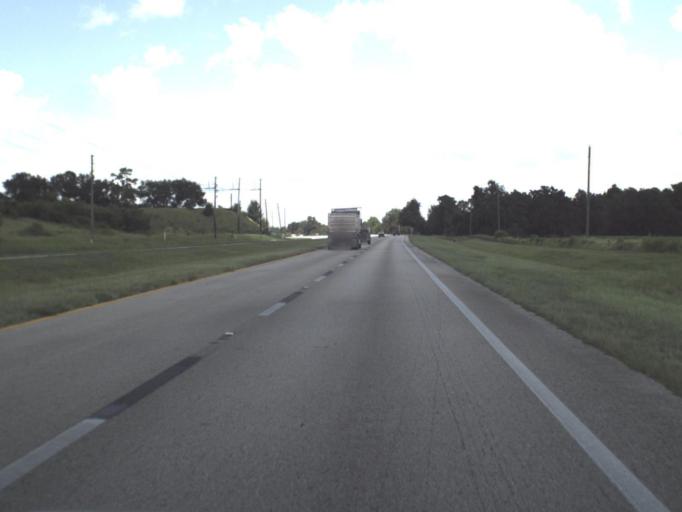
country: US
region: Florida
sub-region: Polk County
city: Fort Meade
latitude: 27.7198
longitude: -81.8026
